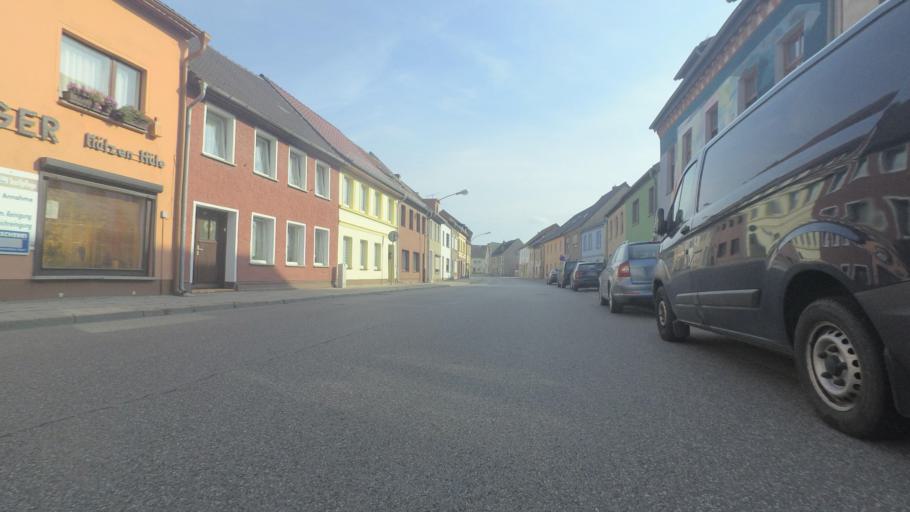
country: DE
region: Mecklenburg-Vorpommern
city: Demmin
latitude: 53.9724
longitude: 13.1296
